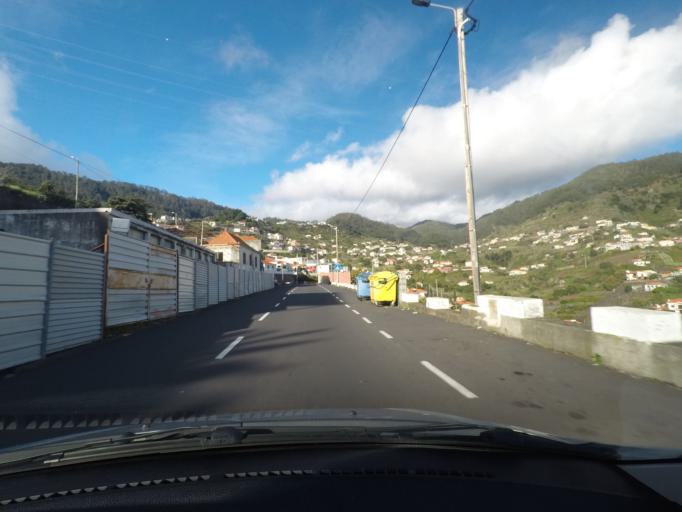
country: PT
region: Madeira
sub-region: Ribeira Brava
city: Campanario
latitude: 32.6706
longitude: -17.0301
